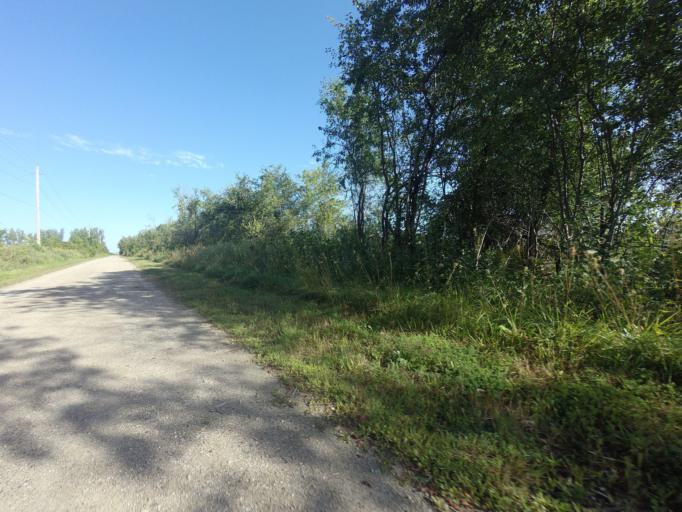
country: CA
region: Ontario
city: Waterloo
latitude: 43.6662
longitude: -80.4372
